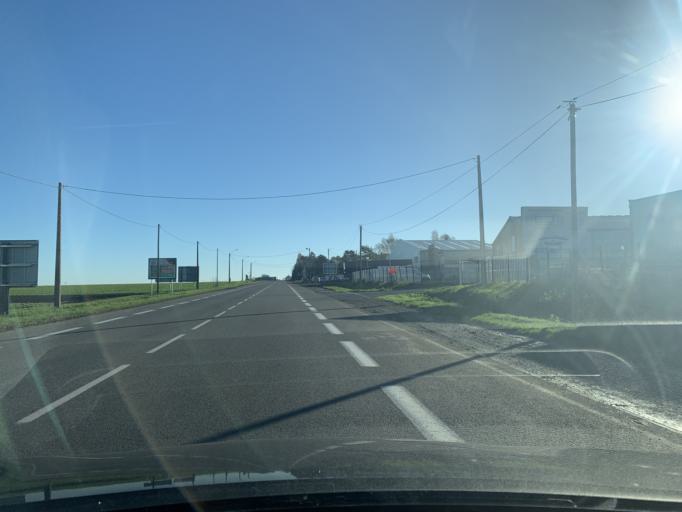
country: FR
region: Nord-Pas-de-Calais
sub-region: Departement du Nord
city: Escaudoeuvres
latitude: 50.1660
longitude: 3.2725
